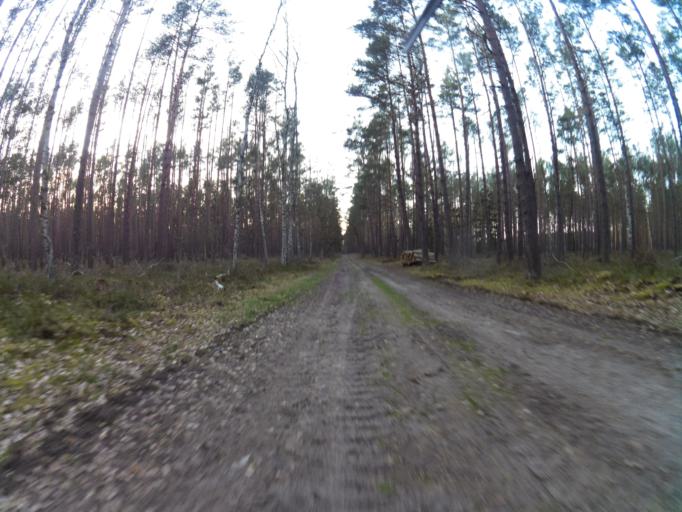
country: PL
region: West Pomeranian Voivodeship
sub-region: Powiat policki
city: Nowe Warpno
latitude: 53.6913
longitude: 14.3293
